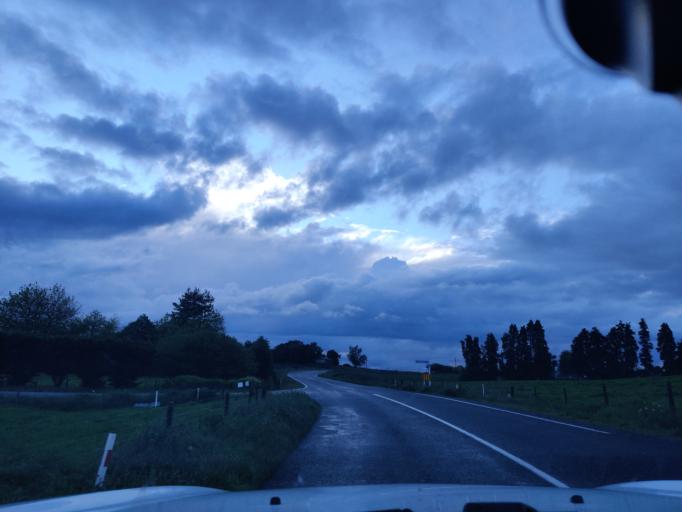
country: NZ
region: Waikato
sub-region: South Waikato District
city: Tokoroa
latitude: -38.2057
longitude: 175.8194
